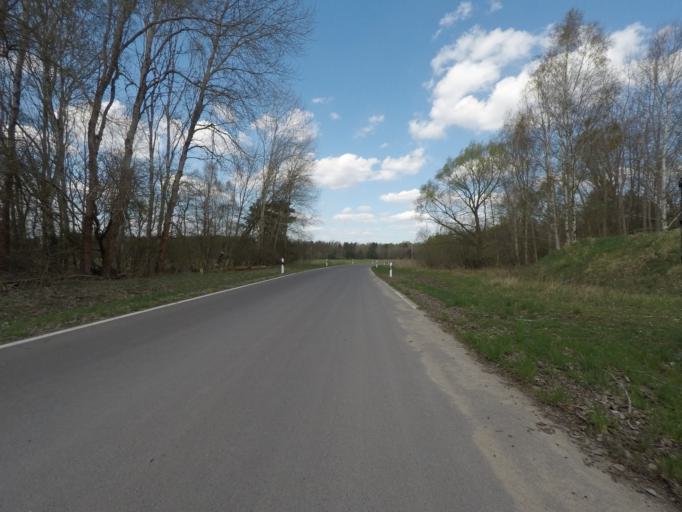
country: DE
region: Brandenburg
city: Melchow
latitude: 52.8319
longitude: 13.6997
